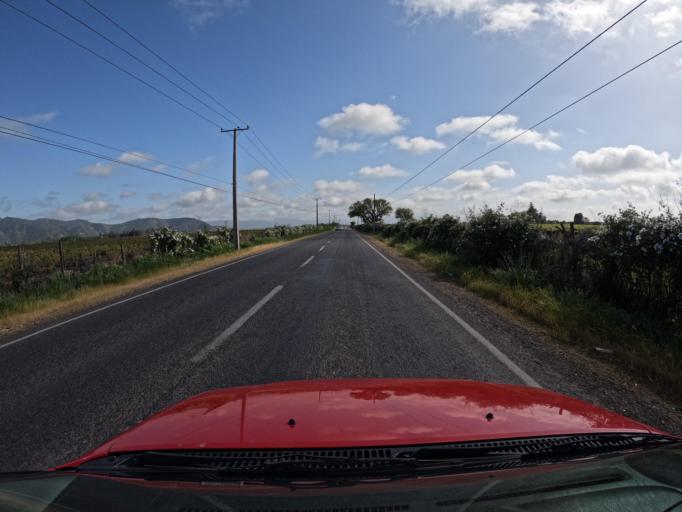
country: CL
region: Maule
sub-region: Provincia de Curico
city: Rauco
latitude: -34.9225
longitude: -71.2769
